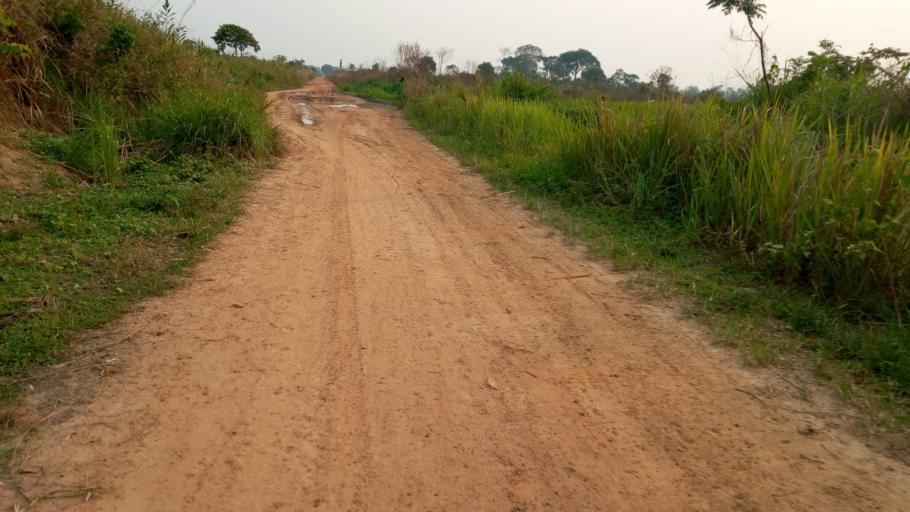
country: CD
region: Bandundu
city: Bandundu
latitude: -3.4222
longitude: 17.6099
